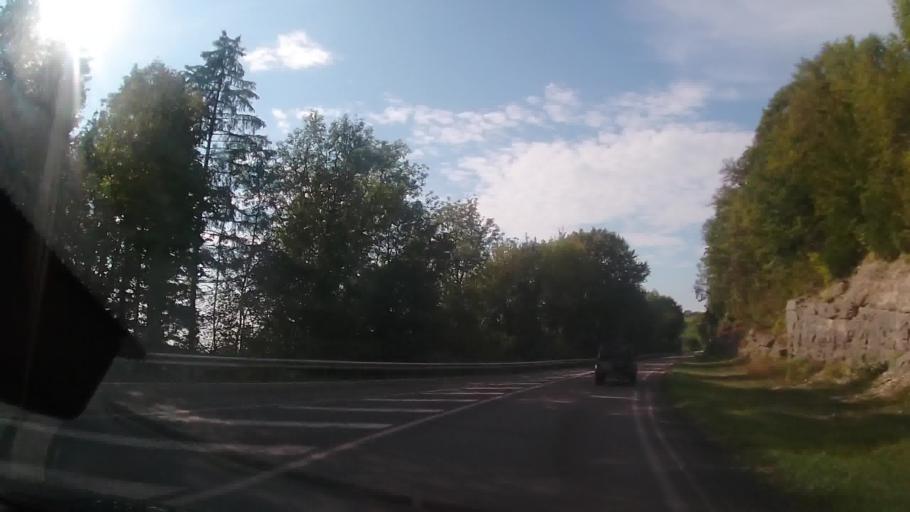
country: FR
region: Franche-Comte
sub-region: Departement du Jura
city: Clairvaux-les-Lacs
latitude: 46.5976
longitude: 5.8700
